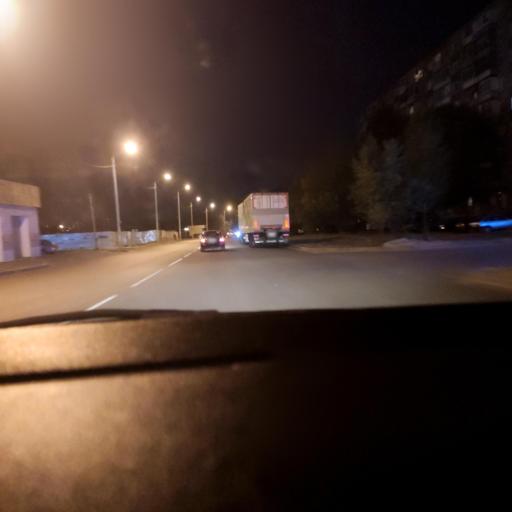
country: RU
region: Voronezj
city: Podgornoye
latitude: 51.7004
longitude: 39.1485
